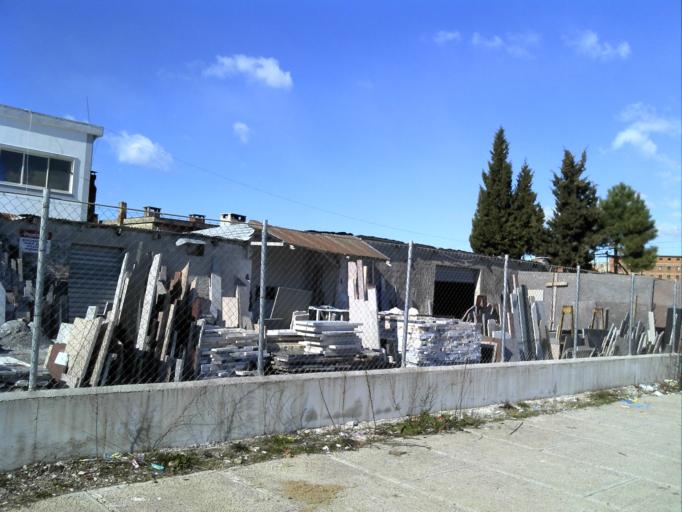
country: AL
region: Shkoder
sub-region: Rrethi i Shkodres
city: Shkoder
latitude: 42.0834
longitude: 19.5301
